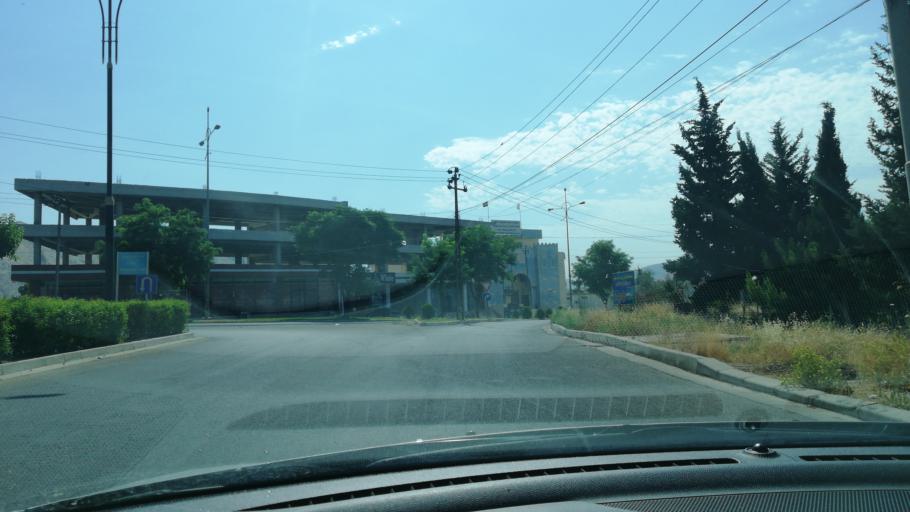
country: IQ
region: Dahuk
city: Dihok
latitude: 36.8624
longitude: 42.9827
